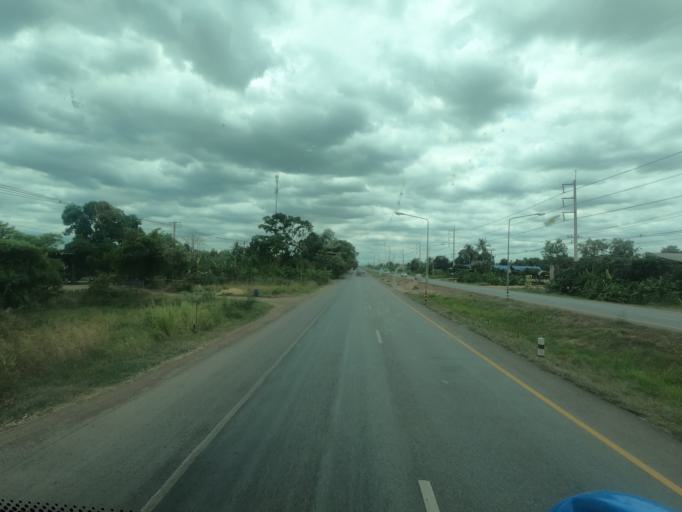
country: TH
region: Nakhon Ratchasima
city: Nong Bun Nak
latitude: 14.7573
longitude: 102.2666
